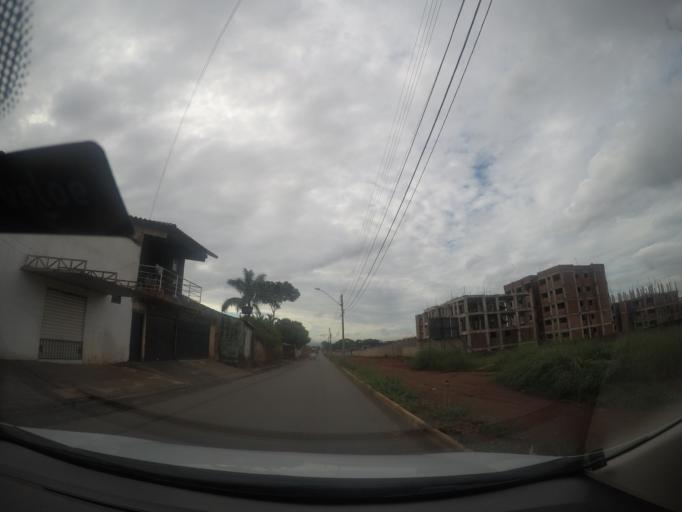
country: BR
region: Goias
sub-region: Goiania
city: Goiania
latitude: -16.6129
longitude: -49.3327
